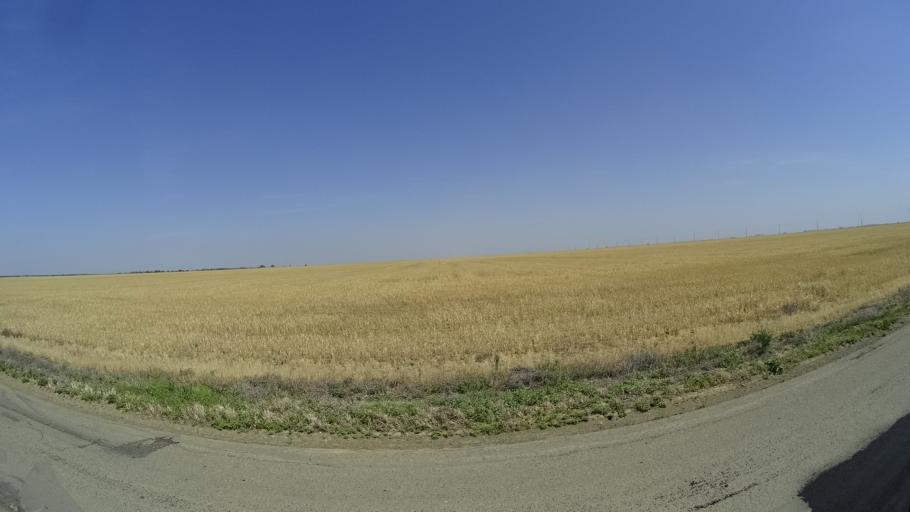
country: US
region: California
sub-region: Kings County
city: Stratford
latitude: 36.1378
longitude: -119.9124
